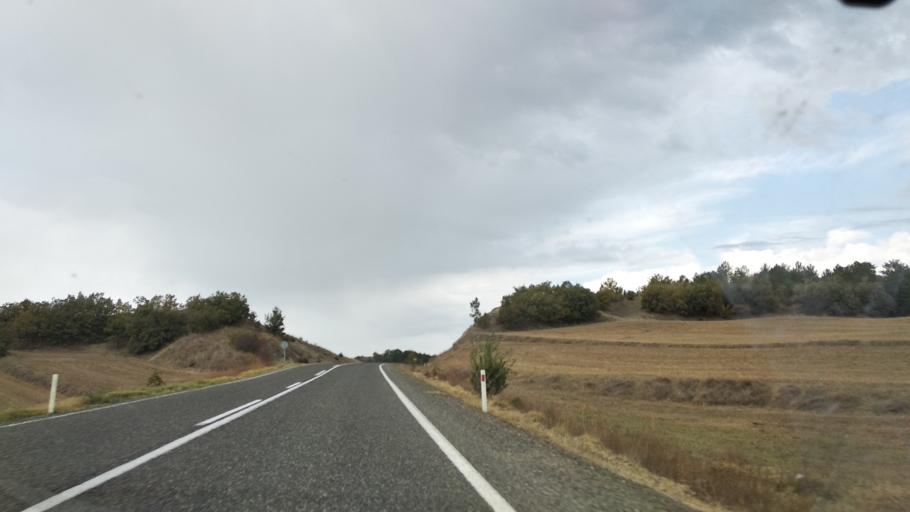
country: TR
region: Bolu
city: Seben
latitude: 40.3327
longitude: 31.4452
